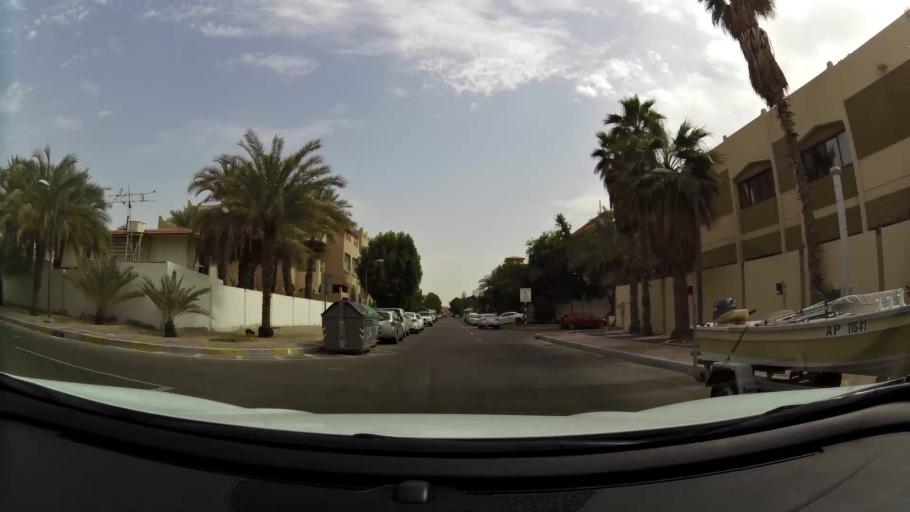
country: AE
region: Abu Dhabi
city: Abu Dhabi
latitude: 24.4598
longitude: 54.3648
